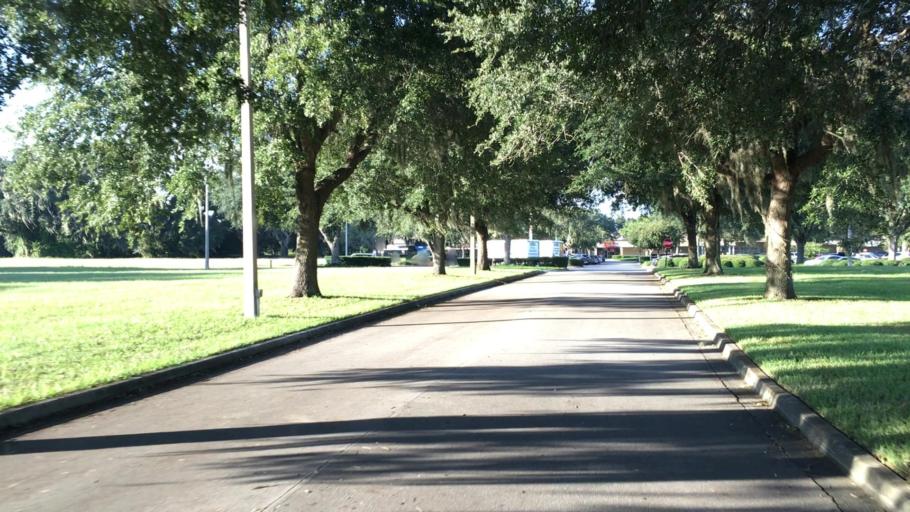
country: US
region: Florida
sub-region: Alachua County
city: Alachua
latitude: 29.6894
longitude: -82.4405
